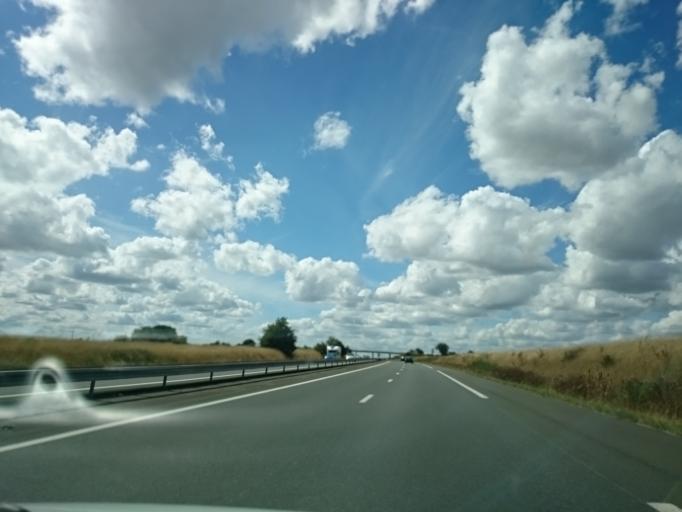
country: FR
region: Pays de la Loire
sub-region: Departement de Maine-et-Loire
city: Saint-Germain-des-Pres
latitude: 47.4375
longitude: -0.8355
